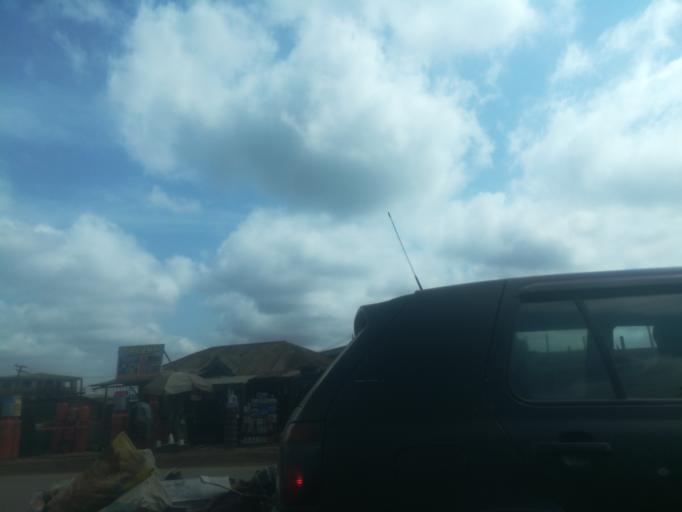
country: NG
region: Oyo
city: Ibadan
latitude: 7.3359
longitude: 3.8557
